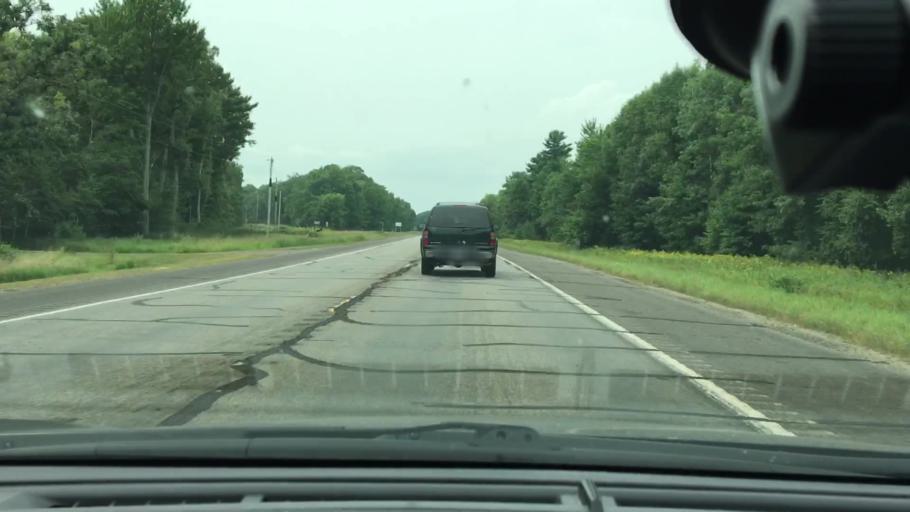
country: US
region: Minnesota
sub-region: Mille Lacs County
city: Vineland
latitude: 46.3259
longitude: -93.7908
